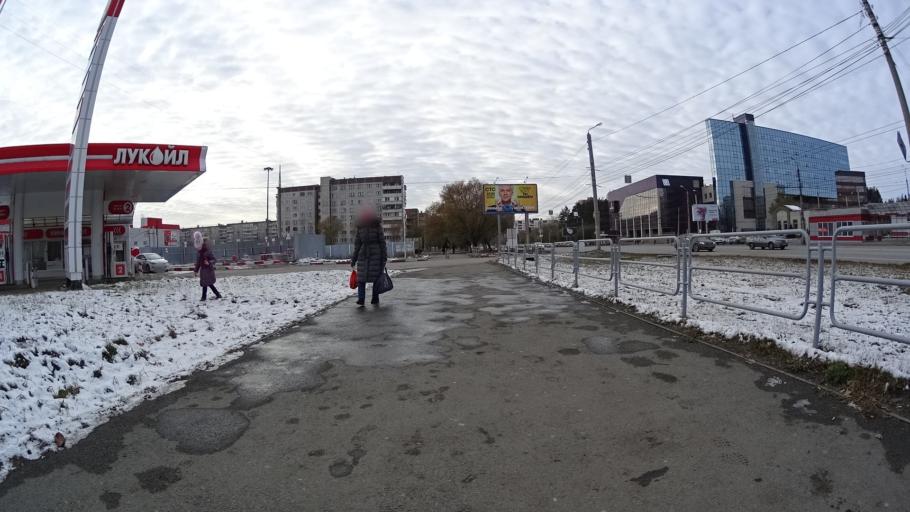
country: RU
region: Chelyabinsk
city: Roshchino
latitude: 55.1934
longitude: 61.3013
